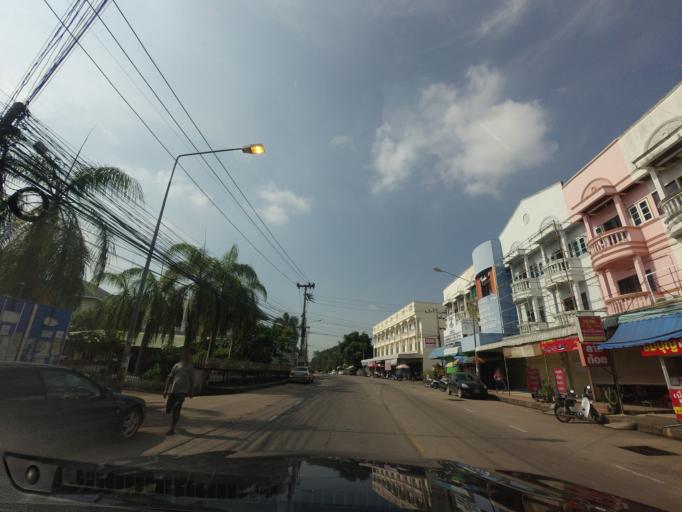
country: TH
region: Khon Kaen
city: Khon Kaen
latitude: 16.4232
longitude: 102.8502
